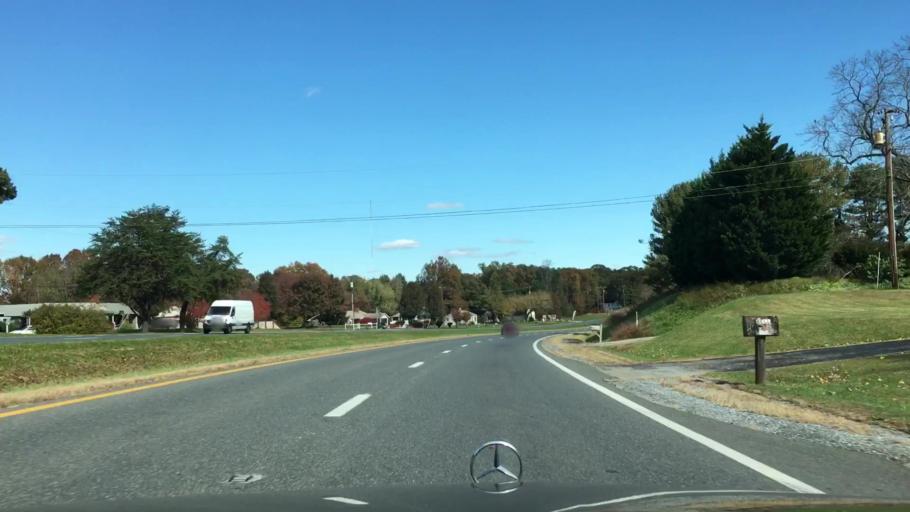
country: US
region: Virginia
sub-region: Campbell County
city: Altavista
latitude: 37.1564
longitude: -79.2266
